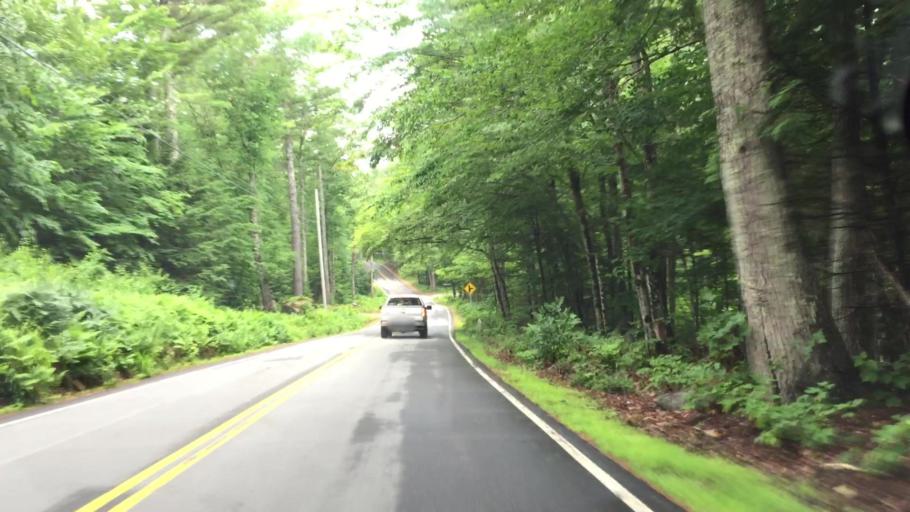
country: US
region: New Hampshire
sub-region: Carroll County
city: Sandwich
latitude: 43.8031
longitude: -71.4855
